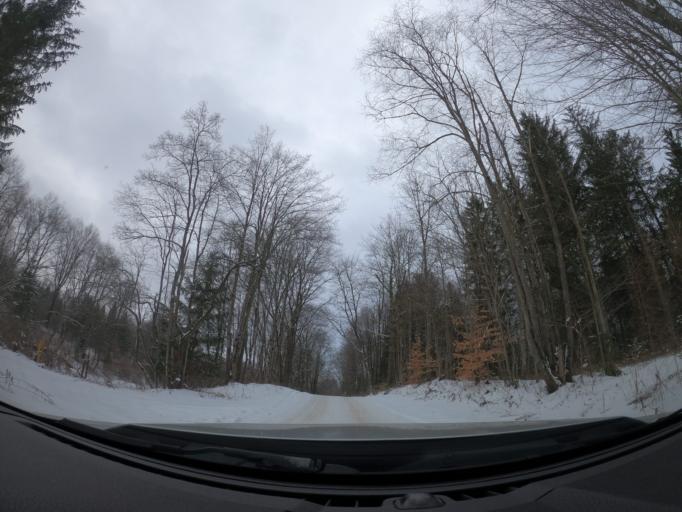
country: US
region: New York
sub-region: Cayuga County
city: Moravia
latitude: 42.7352
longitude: -76.2857
